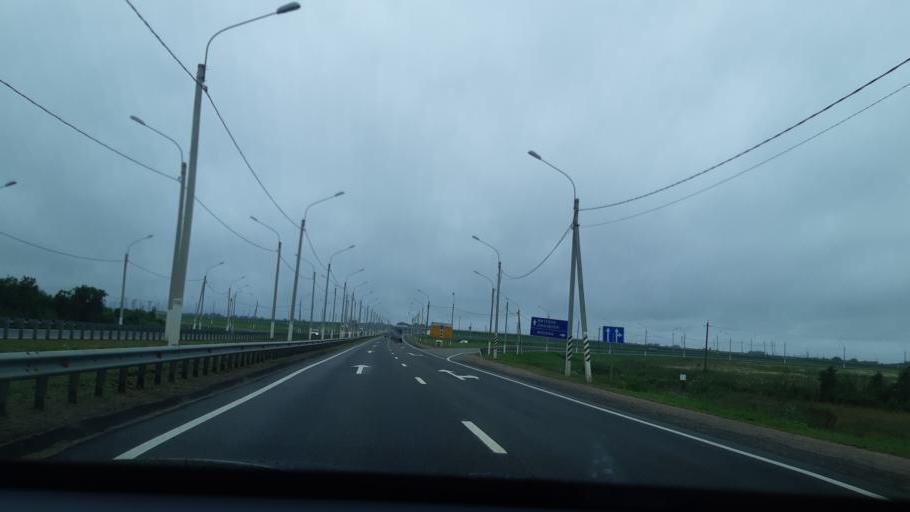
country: RU
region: Smolensk
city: Talashkino
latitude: 54.6999
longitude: 32.1232
